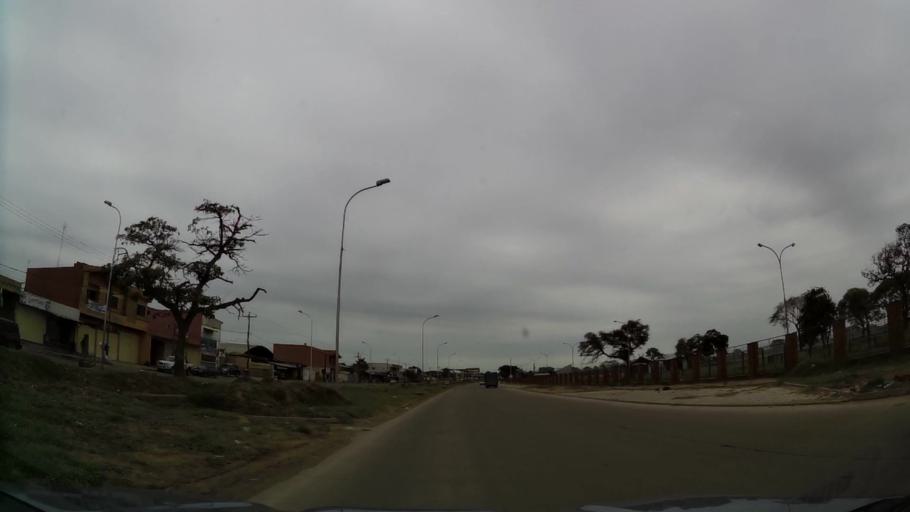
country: BO
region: Santa Cruz
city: Santa Cruz de la Sierra
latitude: -17.8320
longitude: -63.1950
